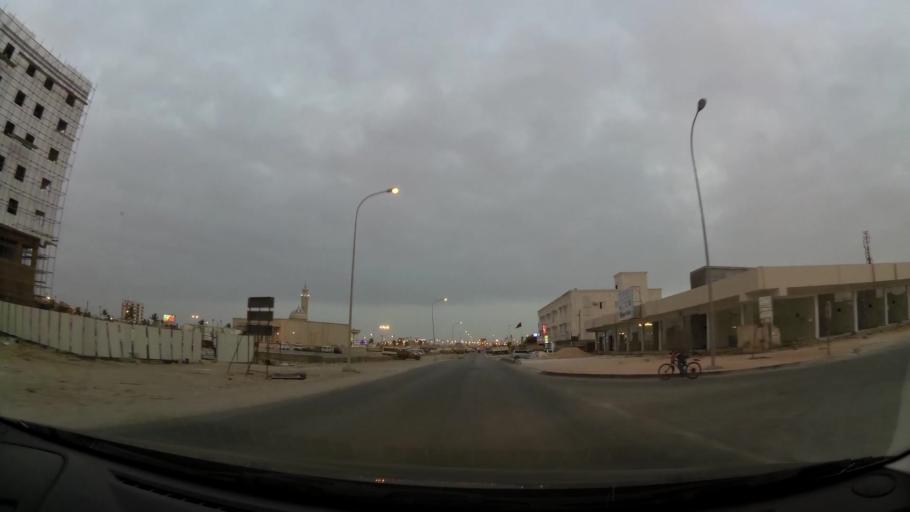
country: OM
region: Zufar
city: Salalah
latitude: 17.0239
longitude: 54.0551
